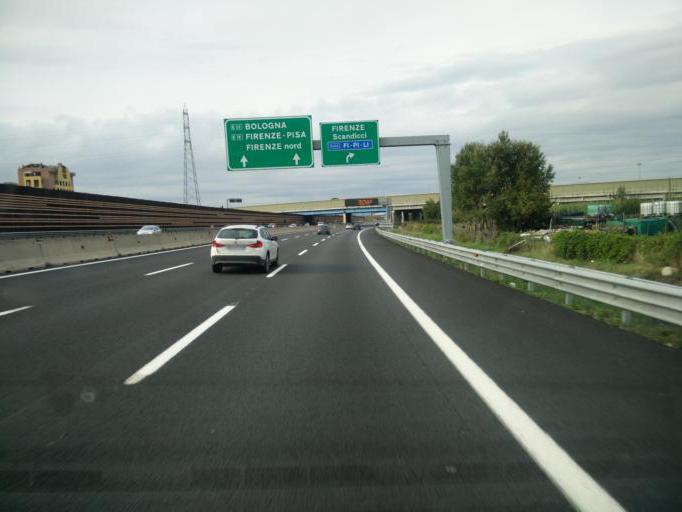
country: IT
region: Tuscany
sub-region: Province of Florence
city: Mantignano-Ugnano
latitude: 43.7708
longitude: 11.1639
